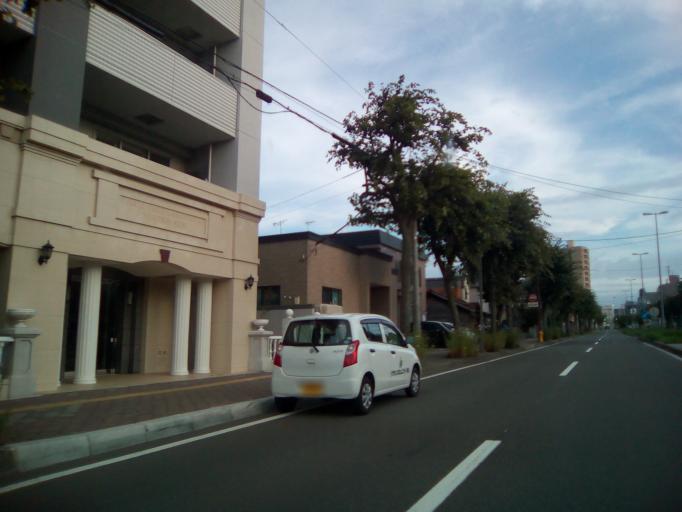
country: JP
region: Hokkaido
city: Sapporo
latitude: 43.0455
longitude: 141.3695
